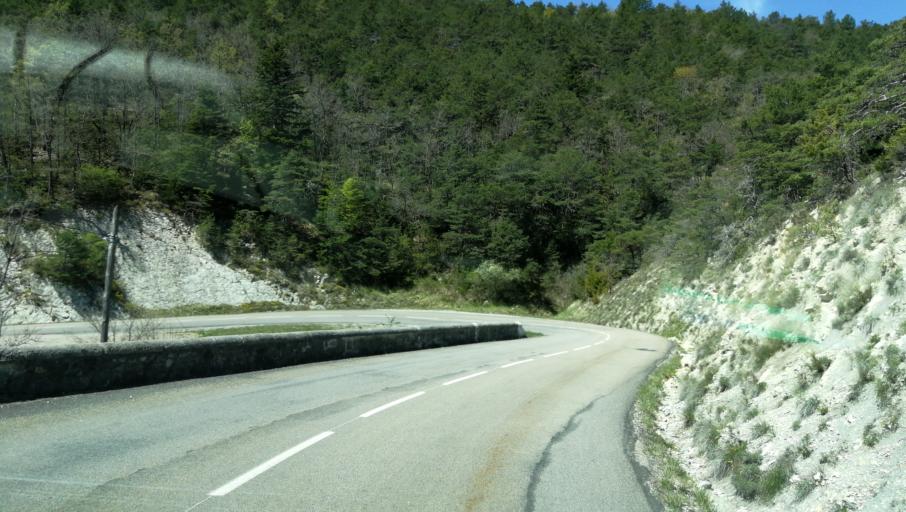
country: FR
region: Rhone-Alpes
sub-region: Departement de la Drome
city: Die
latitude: 44.8064
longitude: 5.3913
